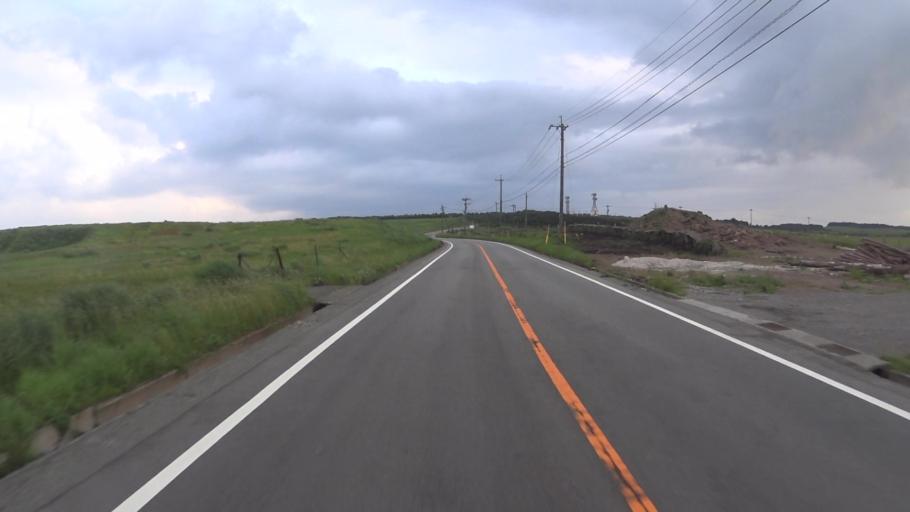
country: JP
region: Kumamoto
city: Aso
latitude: 32.9460
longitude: 130.9794
